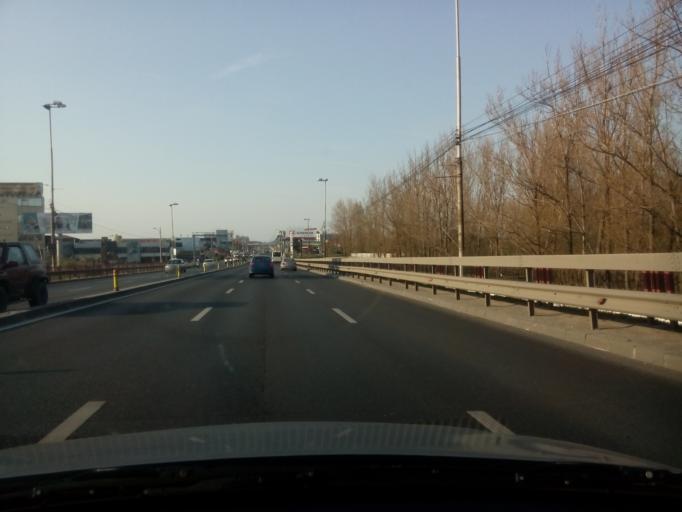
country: RO
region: Ilfov
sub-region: Comuna Otopeni
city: Otopeni
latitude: 44.5366
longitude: 26.0683
